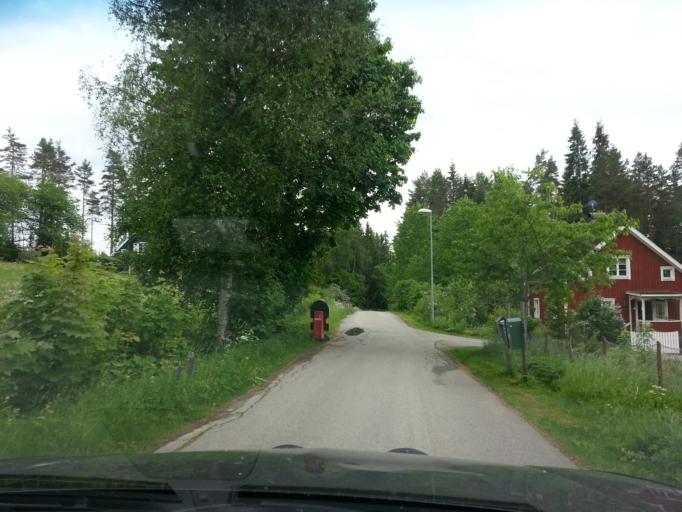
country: SE
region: Joenkoeping
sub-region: Vetlanda Kommun
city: Vetlanda
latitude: 57.2901
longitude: 15.1270
